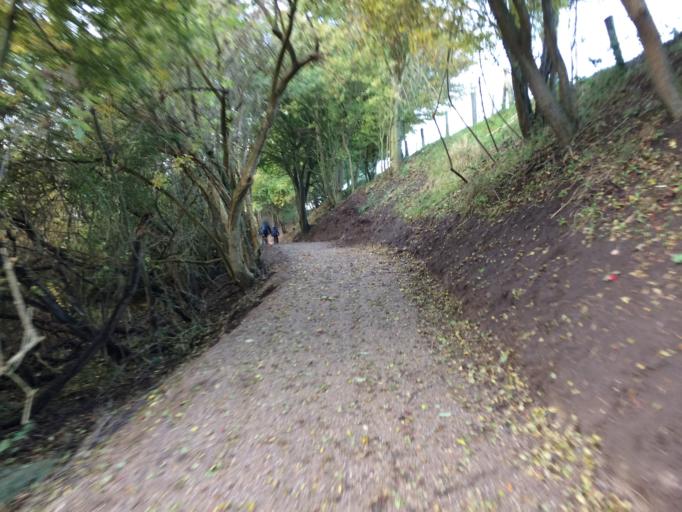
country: DK
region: Zealand
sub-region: Ringsted Kommune
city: Ringsted
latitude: 55.4888
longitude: 11.7609
